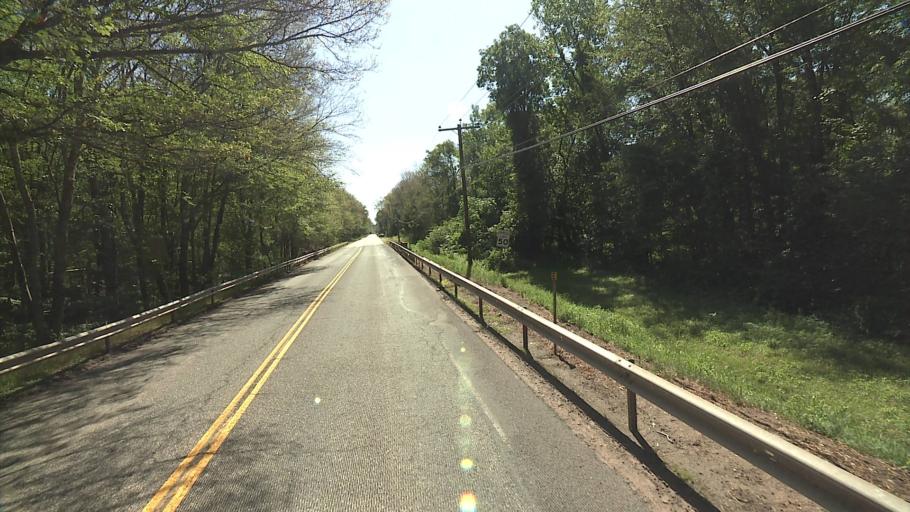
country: US
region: Connecticut
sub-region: Middlesex County
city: East Hampton
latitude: 41.5643
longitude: -72.5281
